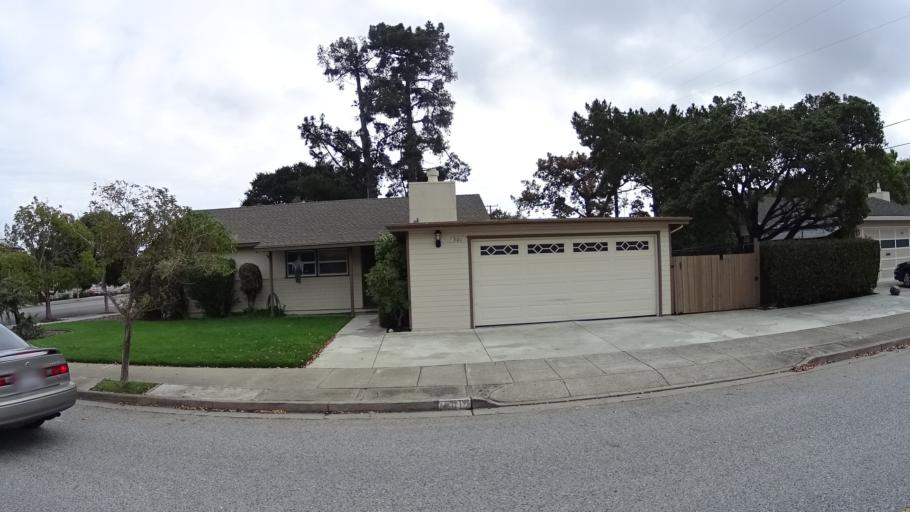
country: US
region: California
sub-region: San Mateo County
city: Belmont
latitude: 37.5303
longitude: -122.2855
